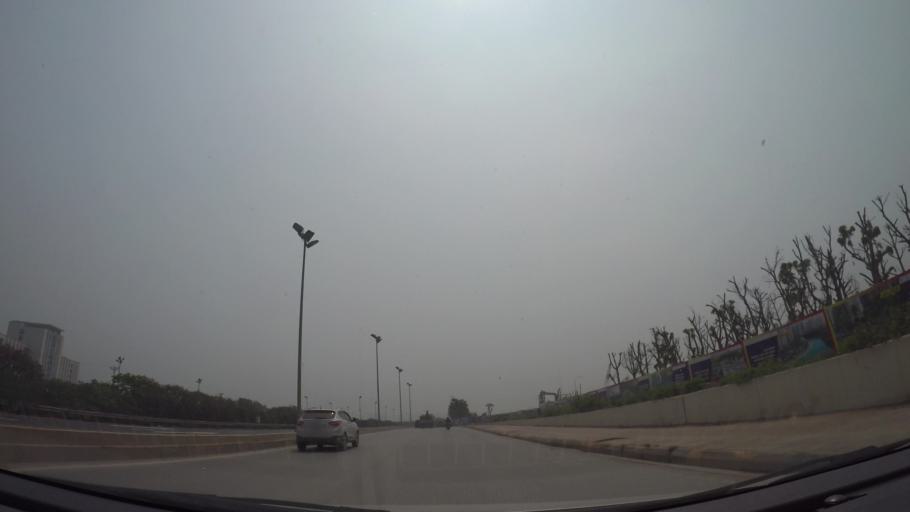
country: VN
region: Ha Noi
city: Cau Dien
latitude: 21.0095
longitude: 105.7435
